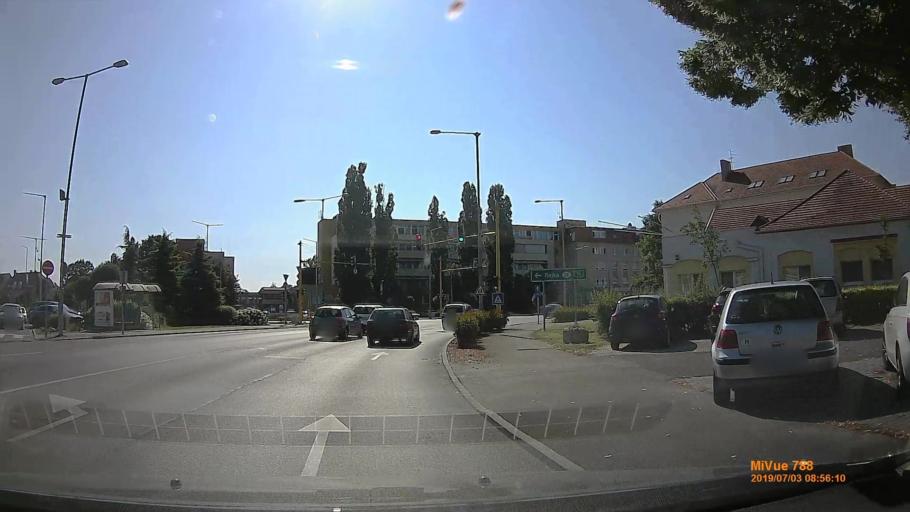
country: HU
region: Gyor-Moson-Sopron
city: Mosonmagyarovar
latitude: 47.8737
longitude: 17.2674
